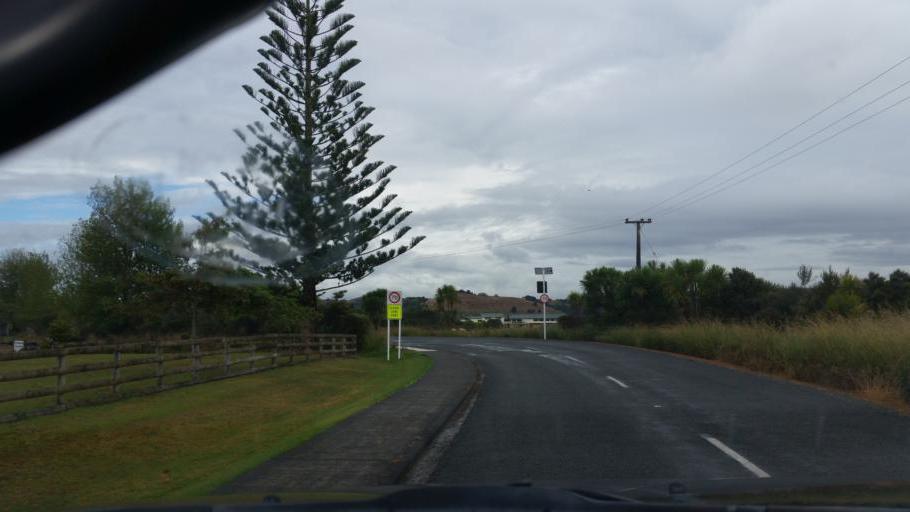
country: NZ
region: Northland
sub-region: Whangarei
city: Ruakaka
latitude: -36.1147
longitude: 174.3655
